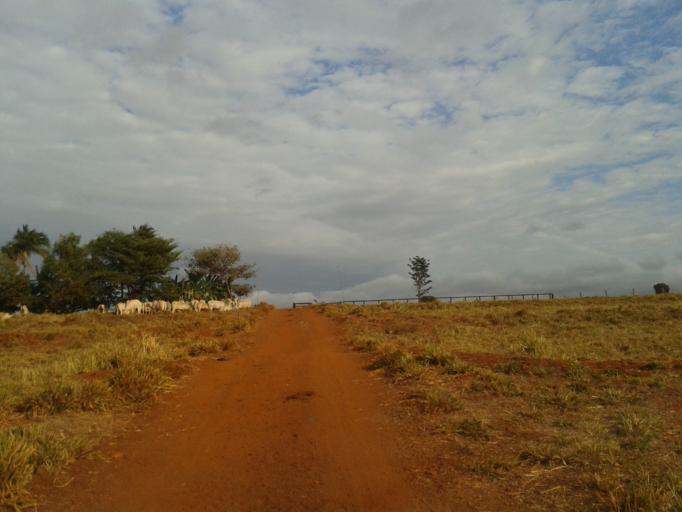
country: BR
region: Minas Gerais
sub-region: Santa Vitoria
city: Santa Vitoria
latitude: -18.7307
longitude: -50.2493
